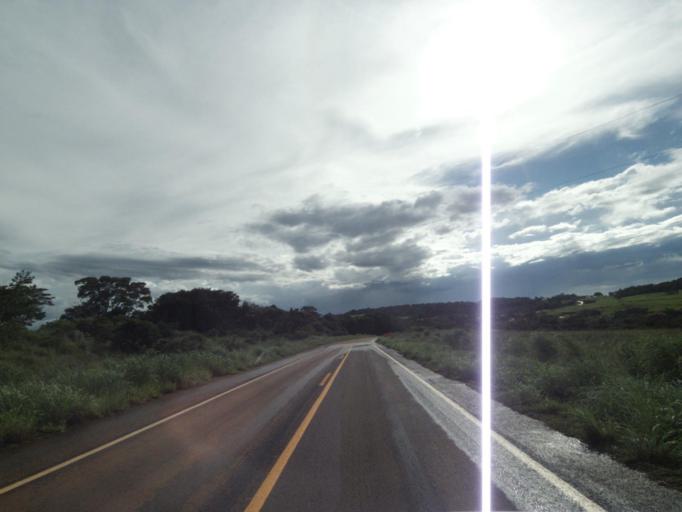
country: BR
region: Goias
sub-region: Jaragua
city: Jaragua
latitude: -15.9078
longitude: -49.5561
